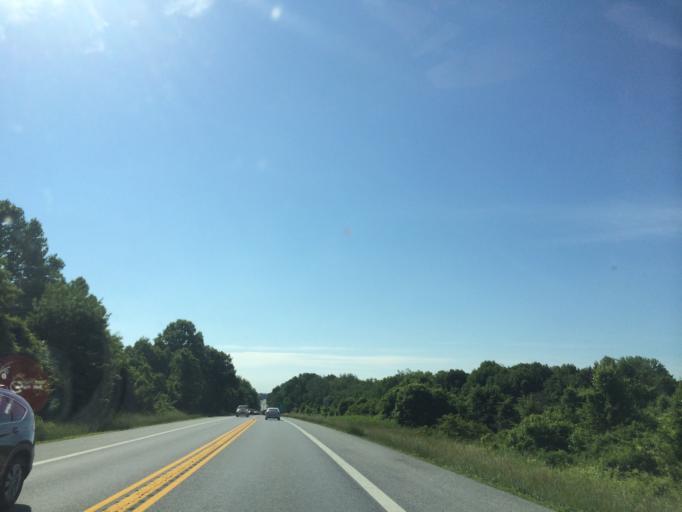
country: US
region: Maryland
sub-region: Howard County
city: Highland
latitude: 39.2190
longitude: -76.9655
